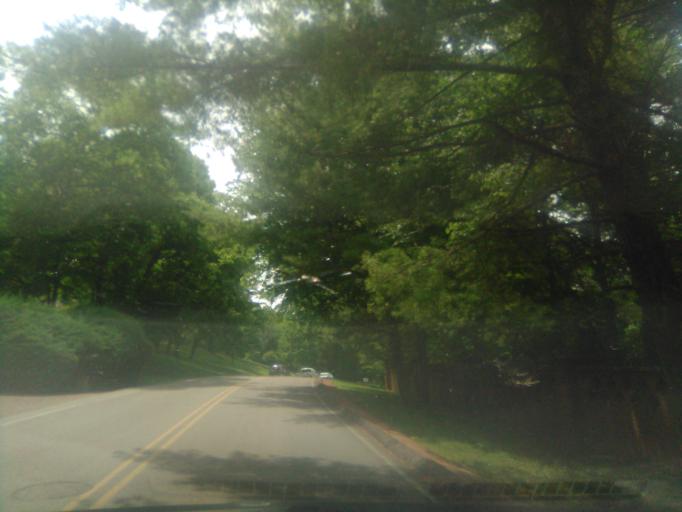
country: US
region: Tennessee
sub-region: Davidson County
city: Forest Hills
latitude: 36.0795
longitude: -86.8502
